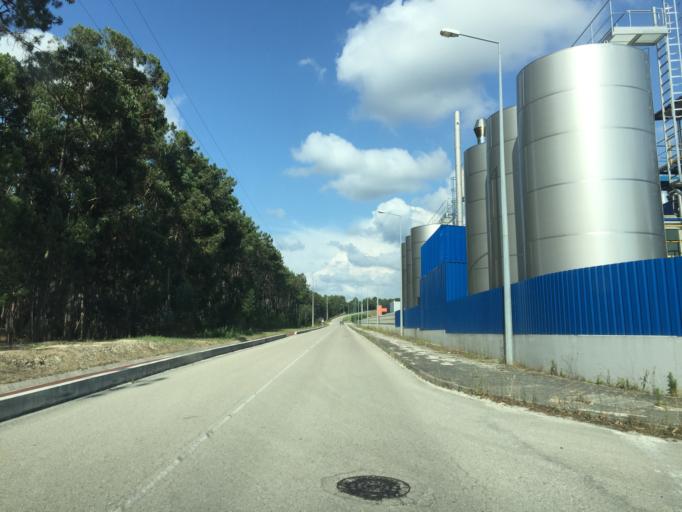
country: PT
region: Leiria
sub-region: Leiria
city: Monte Redondo
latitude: 39.9447
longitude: -8.8098
